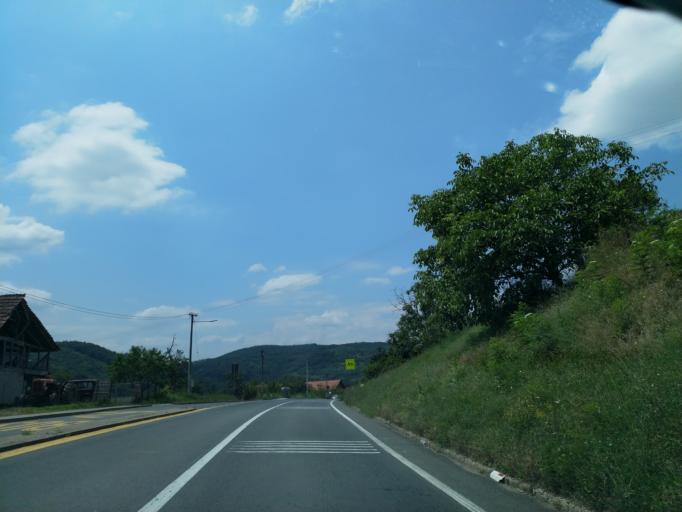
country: RS
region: Central Serbia
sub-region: Rasinski Okrug
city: Aleksandrovac
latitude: 43.4144
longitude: 21.1726
